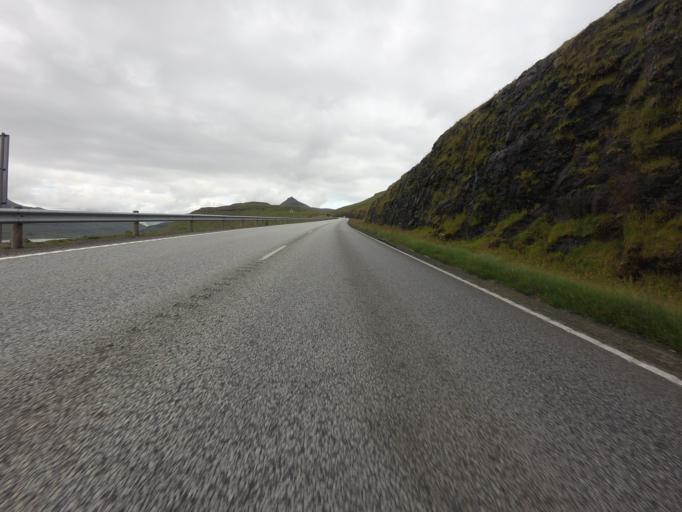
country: FO
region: Eysturoy
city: Eystur
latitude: 62.1700
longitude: -6.7629
